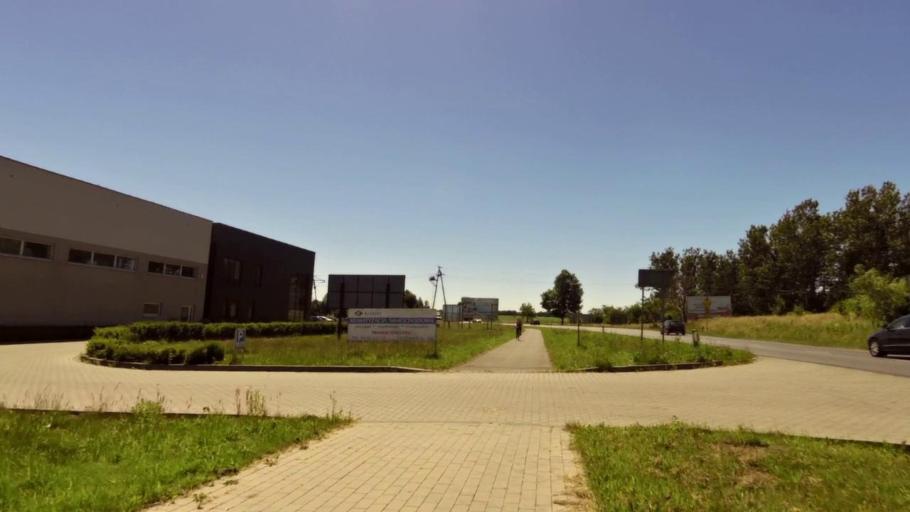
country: PL
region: West Pomeranian Voivodeship
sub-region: Powiat kolobrzeski
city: Kolobrzeg
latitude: 54.1377
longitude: 15.5589
